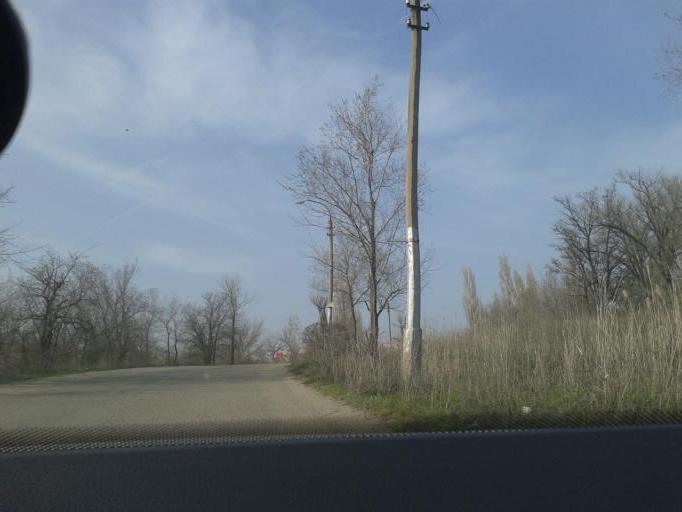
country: RU
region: Volgograd
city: Volgograd
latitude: 48.6312
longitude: 44.4356
